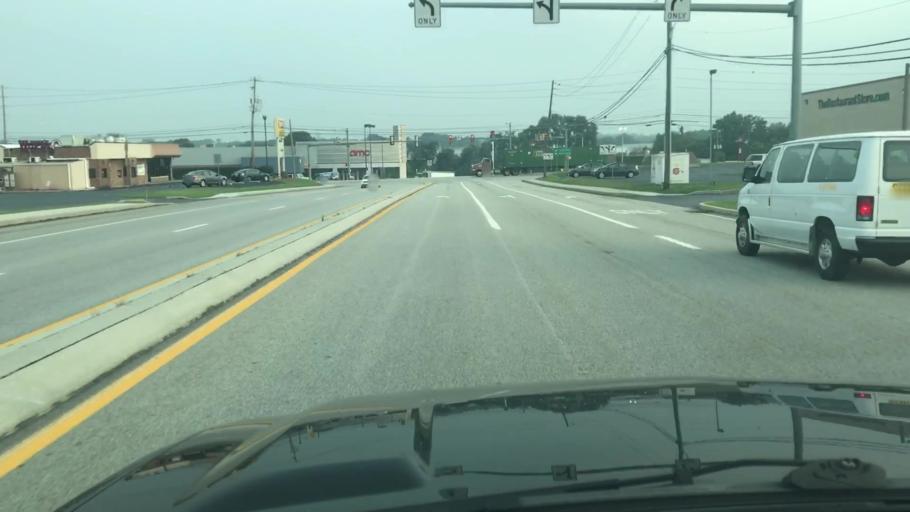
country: US
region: Pennsylvania
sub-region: Cumberland County
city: Shiremanstown
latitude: 40.2252
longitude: -76.9384
